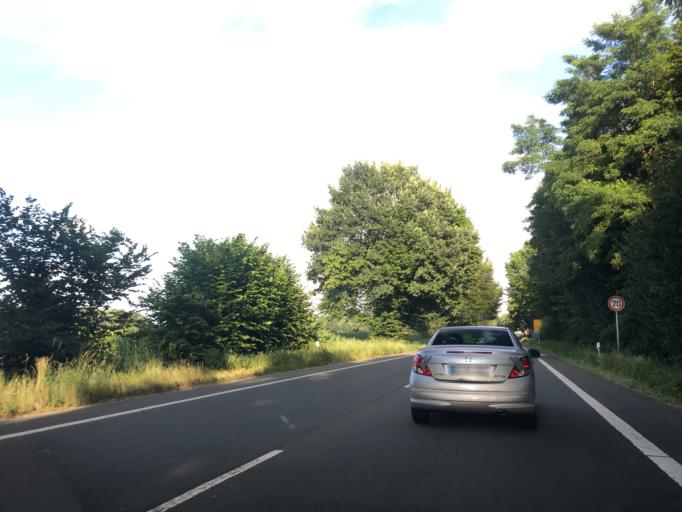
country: DE
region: North Rhine-Westphalia
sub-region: Regierungsbezirk Munster
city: Haltern
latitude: 51.7811
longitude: 7.2039
